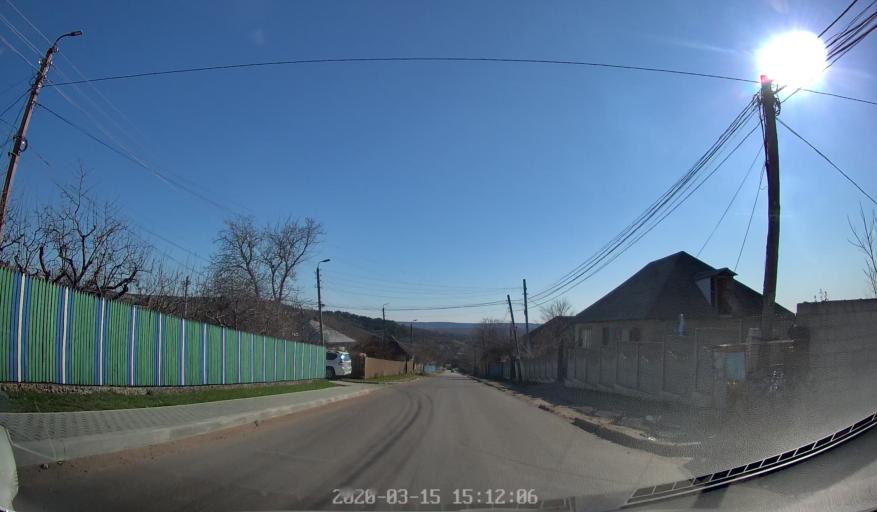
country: MD
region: Orhei
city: Orhei
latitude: 47.2581
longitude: 28.7744
